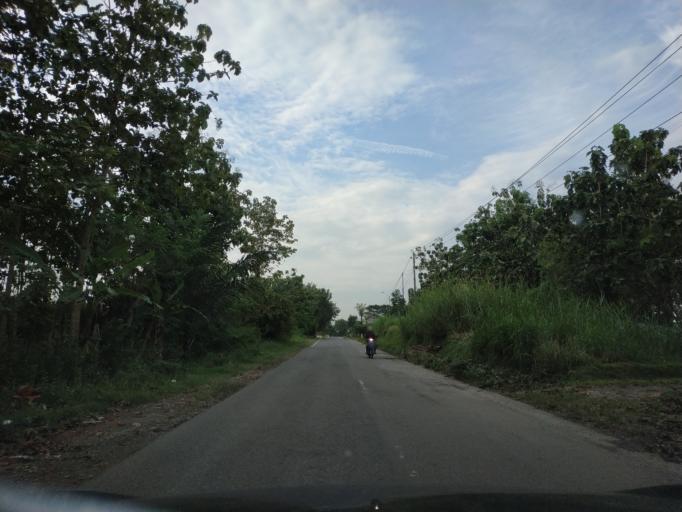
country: ID
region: Central Java
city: Medang
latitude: -6.9097
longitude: 111.4400
